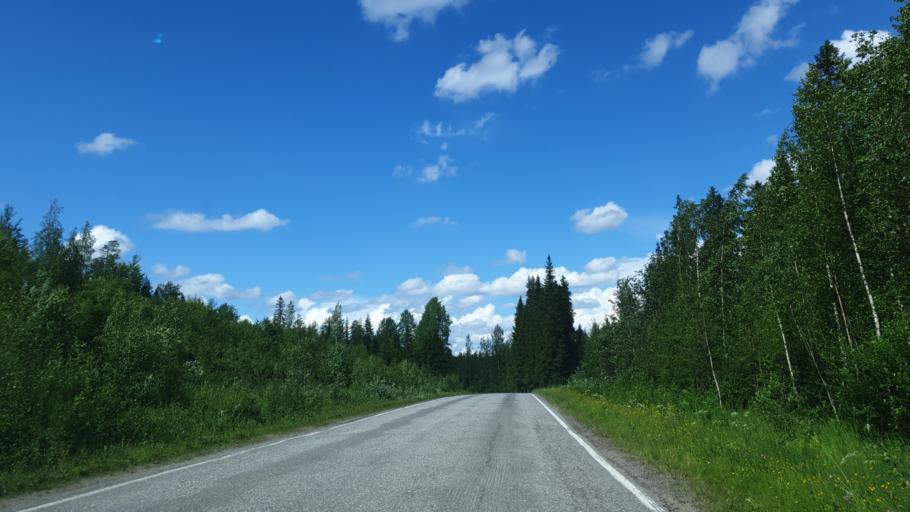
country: FI
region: Northern Savo
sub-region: Koillis-Savo
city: Kaavi
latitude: 63.0311
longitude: 28.6095
